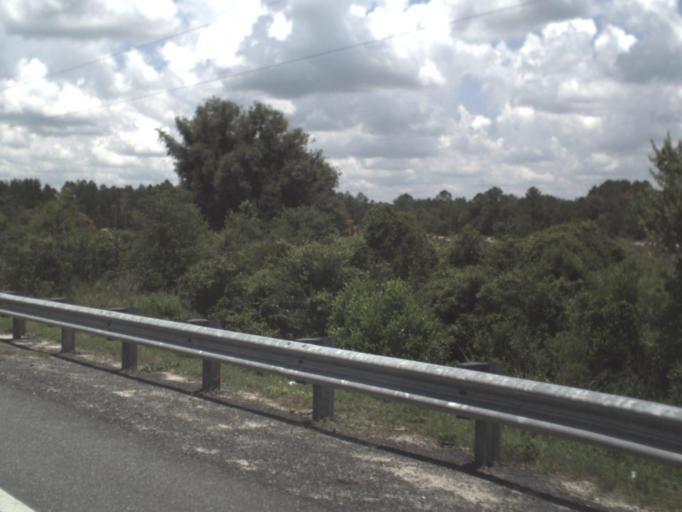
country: US
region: Florida
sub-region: Alachua County
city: Newberry
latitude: 29.6308
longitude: -82.7072
